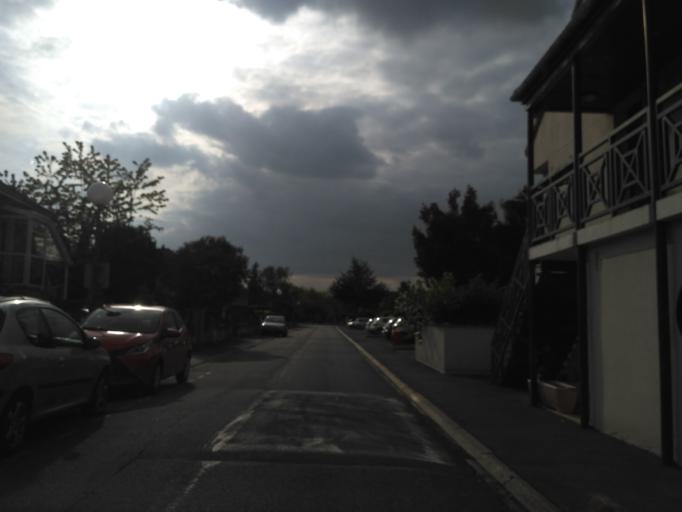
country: FR
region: Ile-de-France
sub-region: Departement de Seine-et-Marne
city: Cesson
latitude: 48.5641
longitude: 2.5972
